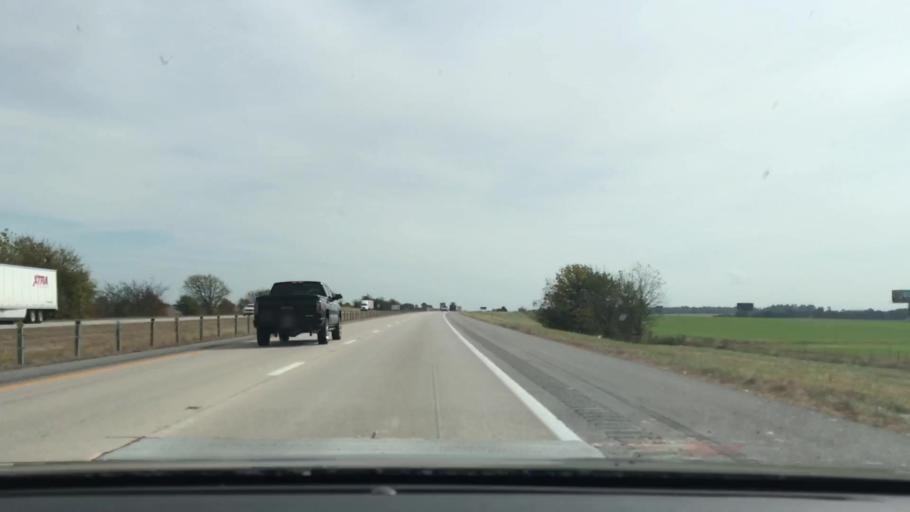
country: US
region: Kentucky
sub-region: Christian County
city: Oak Grove
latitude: 36.6911
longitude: -87.4252
